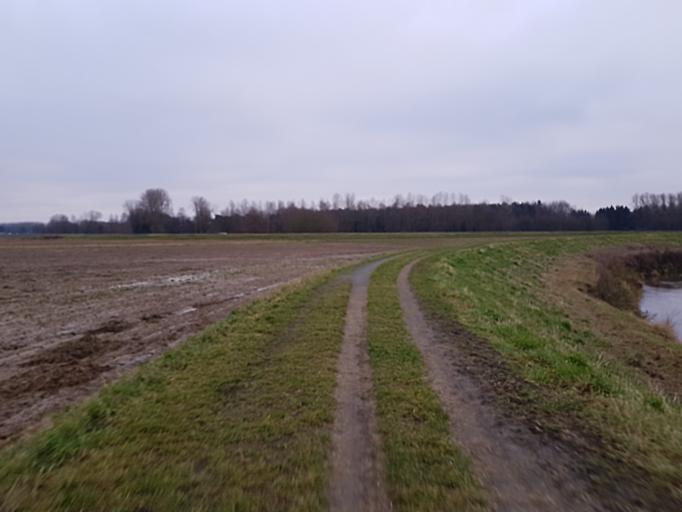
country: BE
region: Flanders
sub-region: Provincie Vlaams-Brabant
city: Tremelo
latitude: 50.9830
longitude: 4.6773
